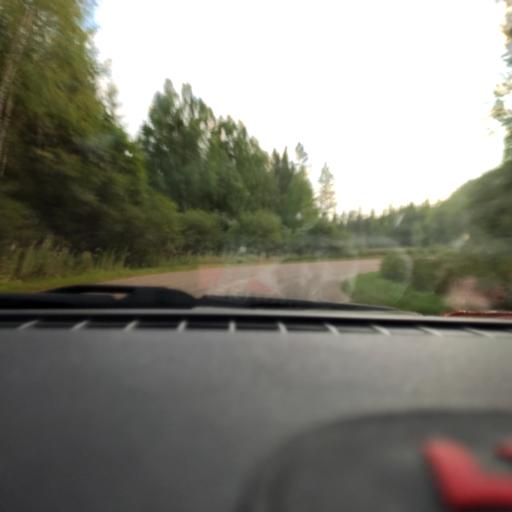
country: RU
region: Perm
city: Pavlovskiy
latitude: 57.9778
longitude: 54.8478
